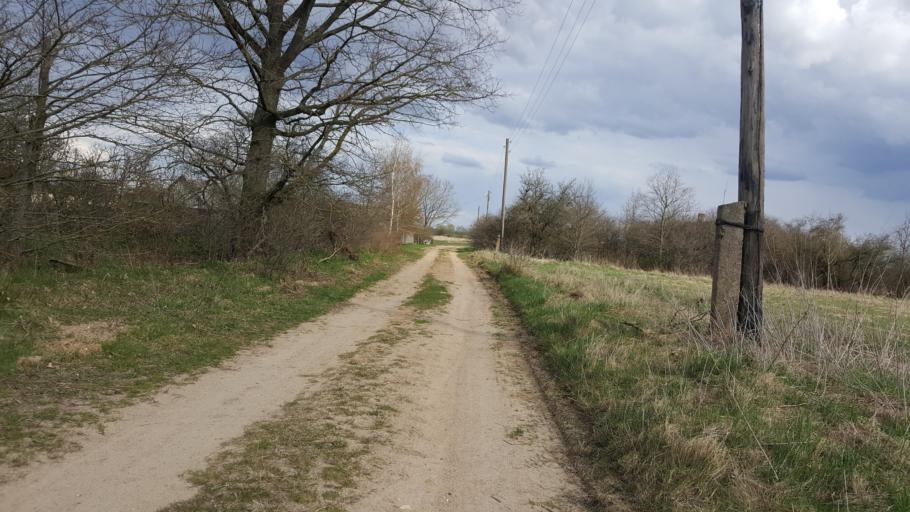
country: BY
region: Brest
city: Kamyanyets
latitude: 52.4370
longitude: 23.6828
